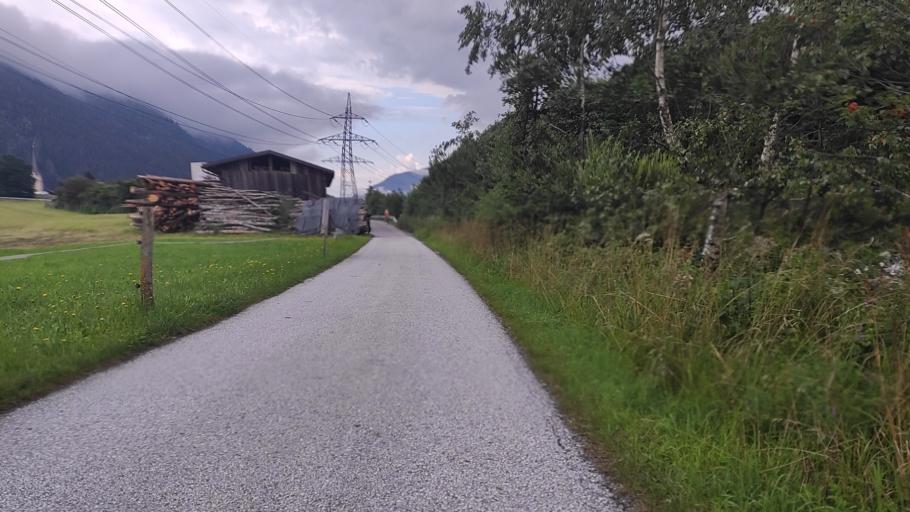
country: AT
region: Salzburg
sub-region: Politischer Bezirk Zell am See
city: Hollersbach im Pinzgau
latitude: 47.2787
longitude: 12.4261
